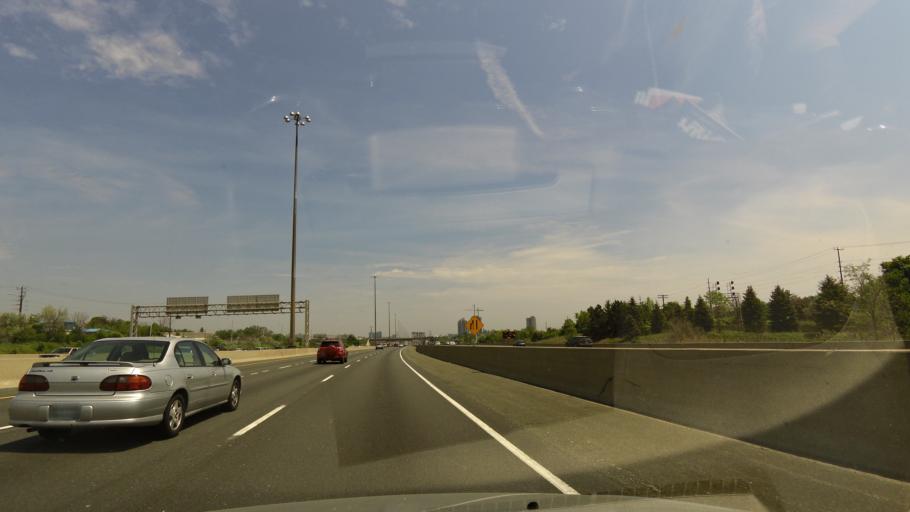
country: CA
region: Ontario
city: Ajax
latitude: 43.8225
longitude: -79.1057
